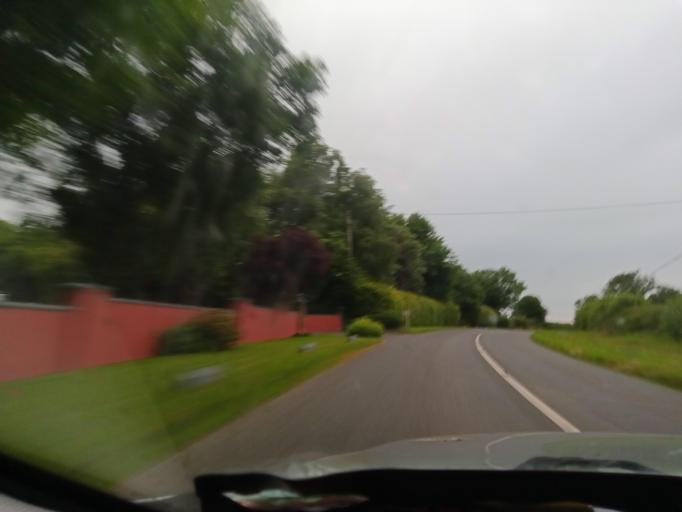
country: IE
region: Leinster
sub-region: Laois
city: Mountmellick
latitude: 53.1250
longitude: -7.3828
